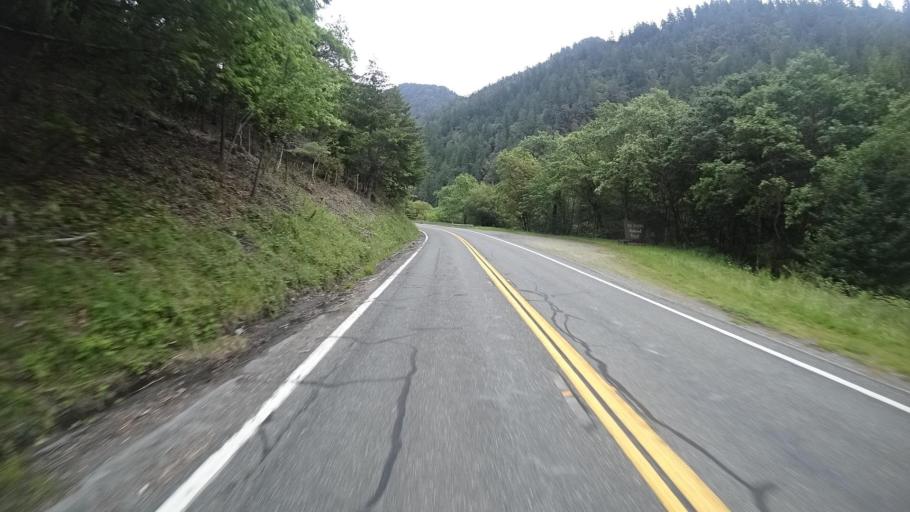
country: US
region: California
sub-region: Humboldt County
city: Willow Creek
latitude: 41.2094
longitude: -123.6582
